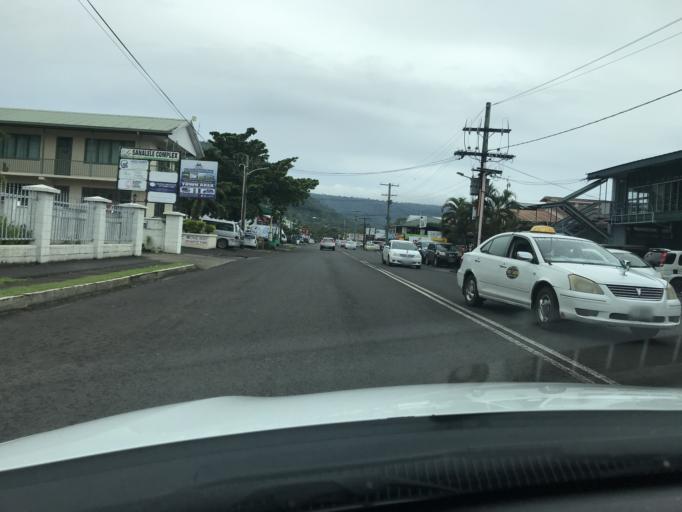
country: WS
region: Tuamasaga
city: Apia
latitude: -13.8342
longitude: -171.7699
